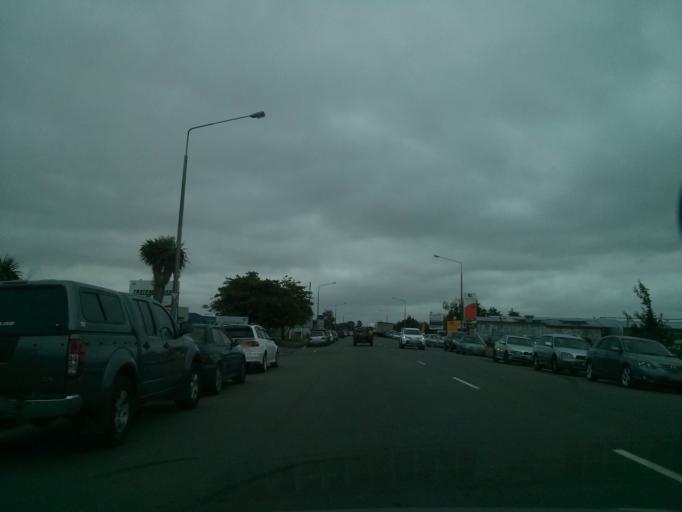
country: NZ
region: Canterbury
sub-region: Selwyn District
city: Prebbleton
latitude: -43.5374
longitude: 172.5421
